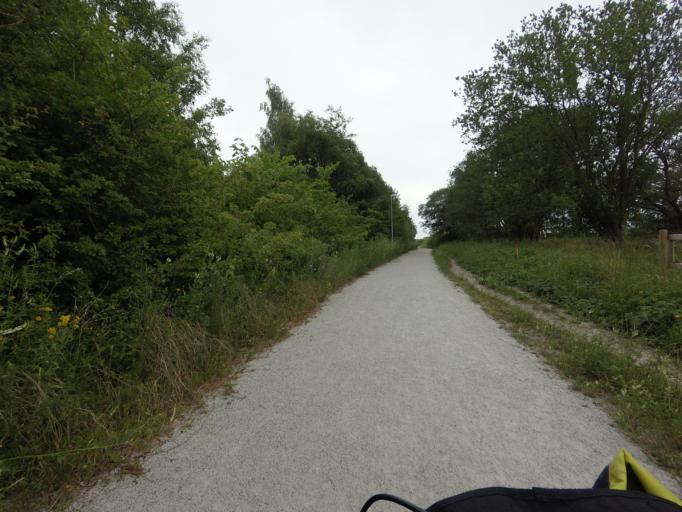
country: SE
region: Skane
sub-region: Malmo
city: Bunkeflostrand
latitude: 55.5242
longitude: 12.9219
